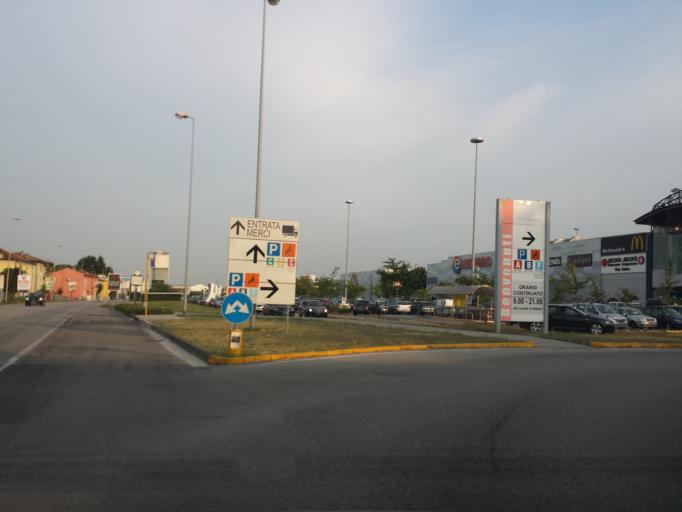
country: IT
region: Veneto
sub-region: Provincia di Vicenza
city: Villaggio Montegrappa
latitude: 45.5302
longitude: 11.5955
